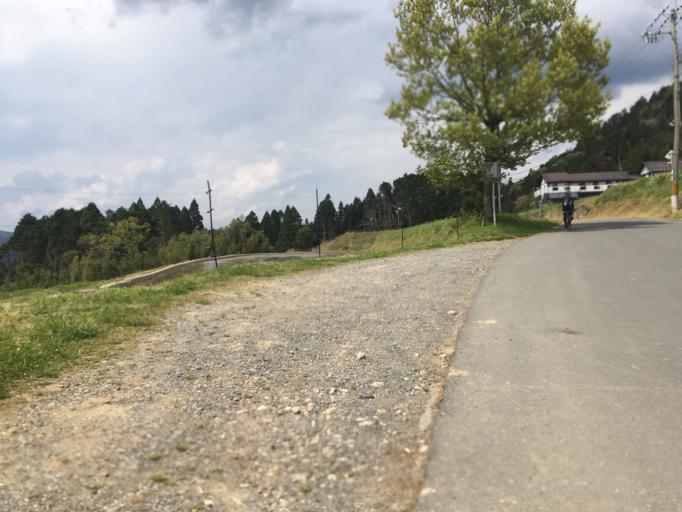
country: JP
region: Kyoto
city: Kameoka
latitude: 35.0749
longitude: 135.6108
